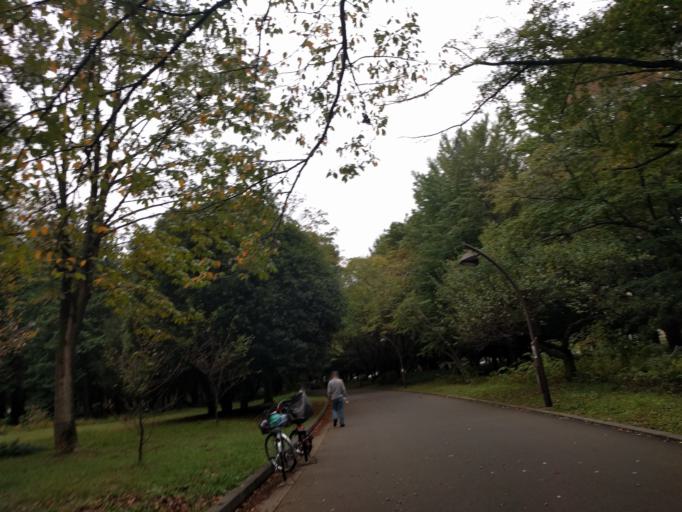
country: JP
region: Saitama
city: Wako
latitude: 35.7686
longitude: 139.6261
